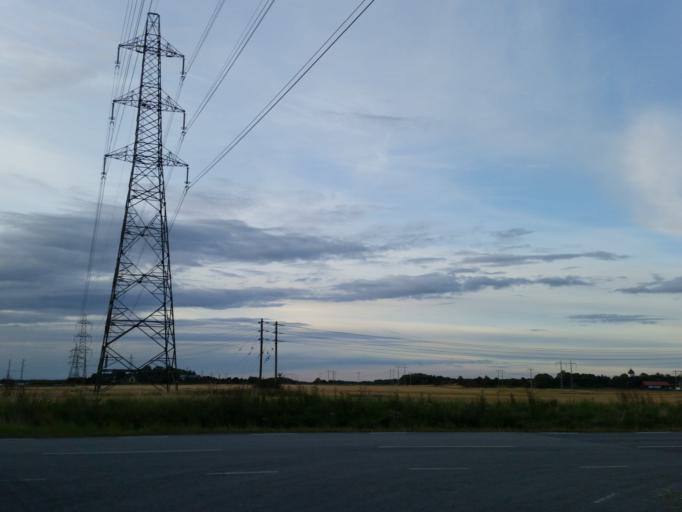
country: SE
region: Stockholm
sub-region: Sigtuna Kommun
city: Marsta
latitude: 59.6303
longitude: 17.8743
